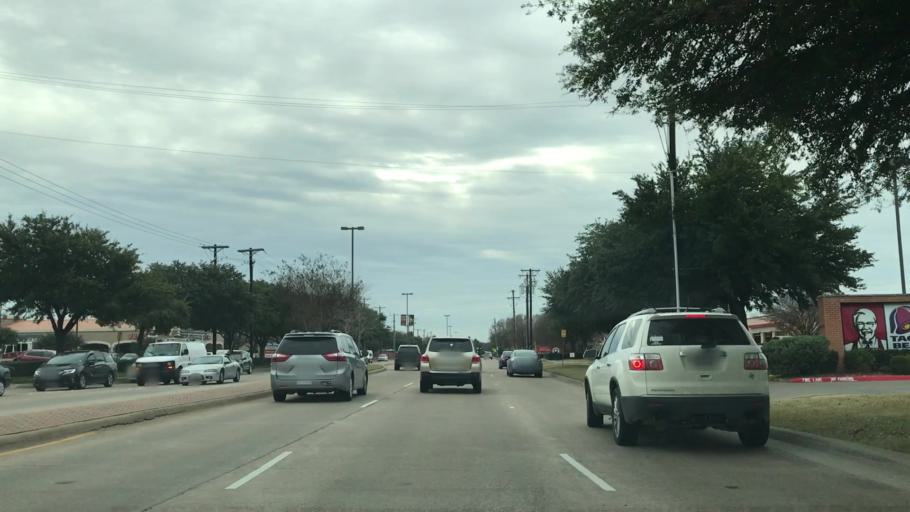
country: US
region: Texas
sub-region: Denton County
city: The Colony
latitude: 33.0242
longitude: -96.8850
